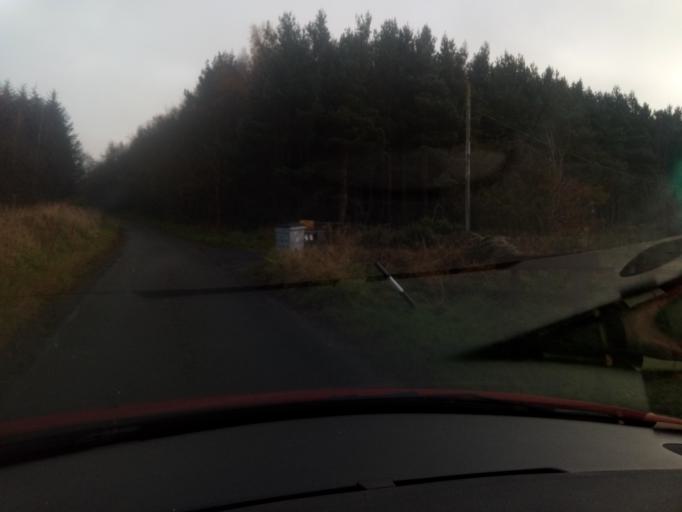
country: GB
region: Scotland
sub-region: The Scottish Borders
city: Jedburgh
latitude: 55.4855
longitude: -2.5915
